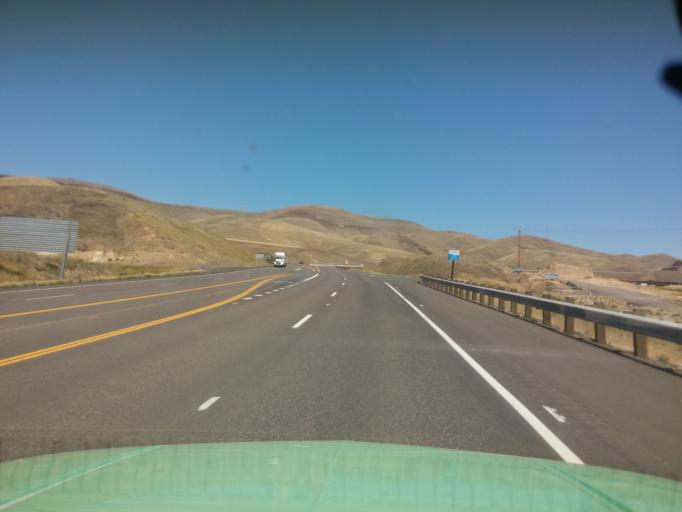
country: US
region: Idaho
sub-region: Nez Perce County
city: Lewiston
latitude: 46.4392
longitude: -116.9858
